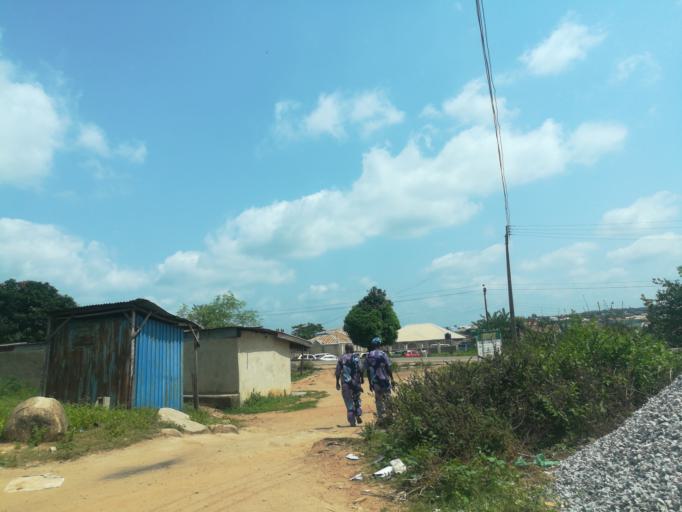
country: NG
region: Oyo
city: Moniya
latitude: 7.5383
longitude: 3.9110
